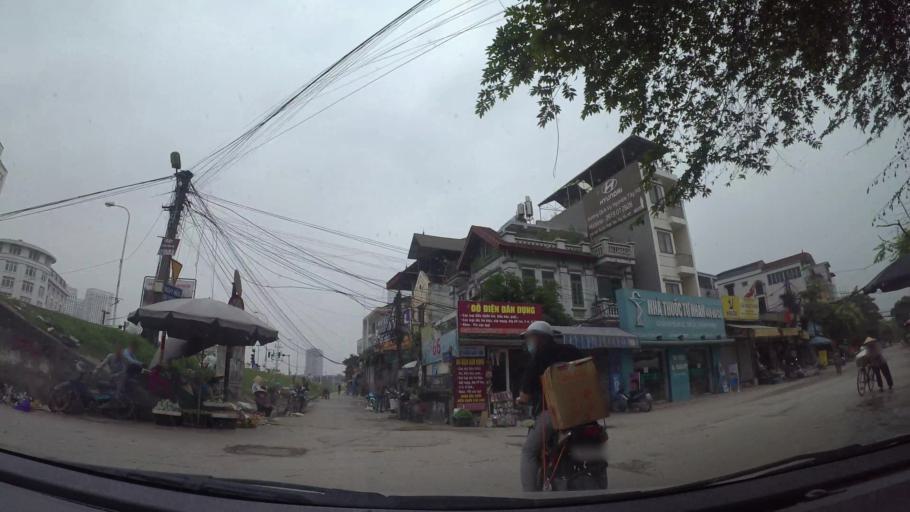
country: VN
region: Ha Noi
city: Tay Ho
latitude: 21.0807
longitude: 105.8193
